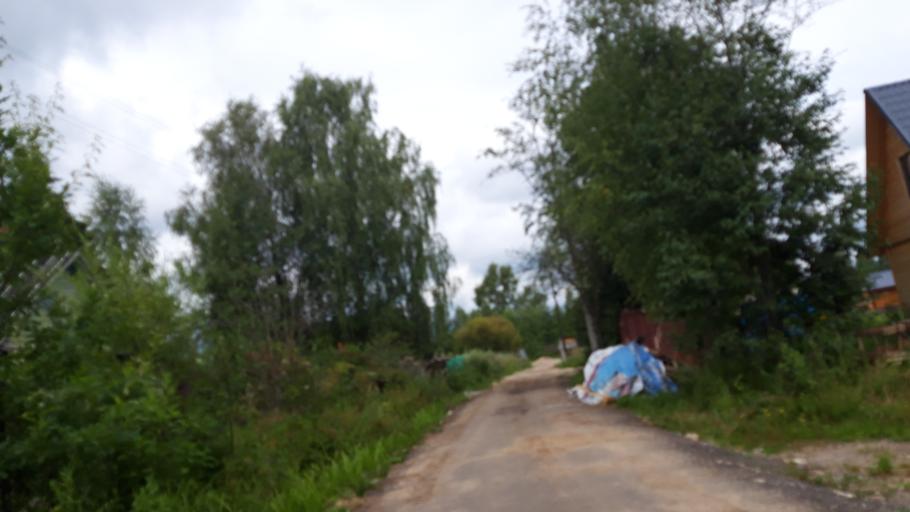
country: RU
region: Tverskaya
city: Konakovo
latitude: 56.6740
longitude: 36.7217
